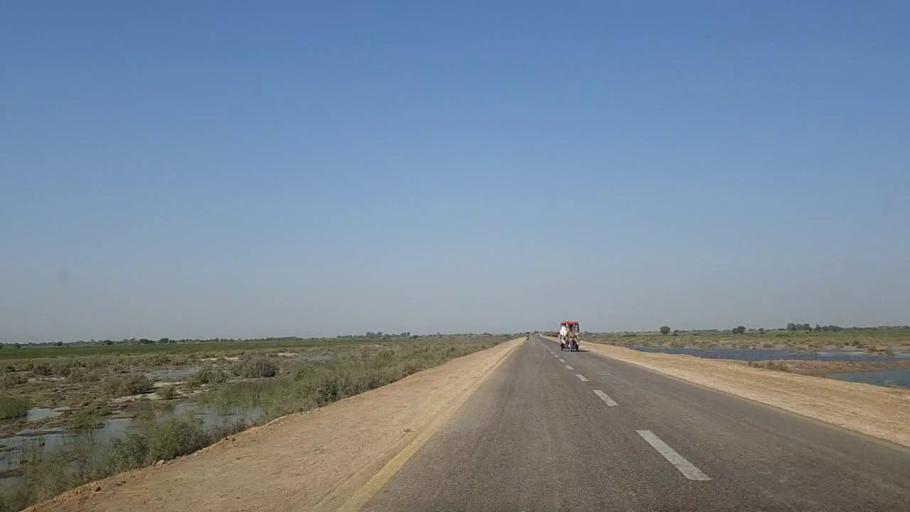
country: PK
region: Sindh
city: Jati
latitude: 24.4010
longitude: 68.2937
